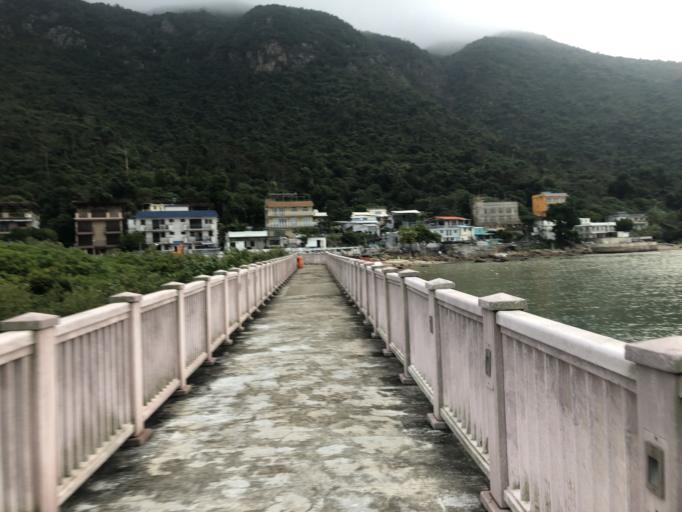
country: HK
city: Tai O
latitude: 22.2476
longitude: 113.8613
